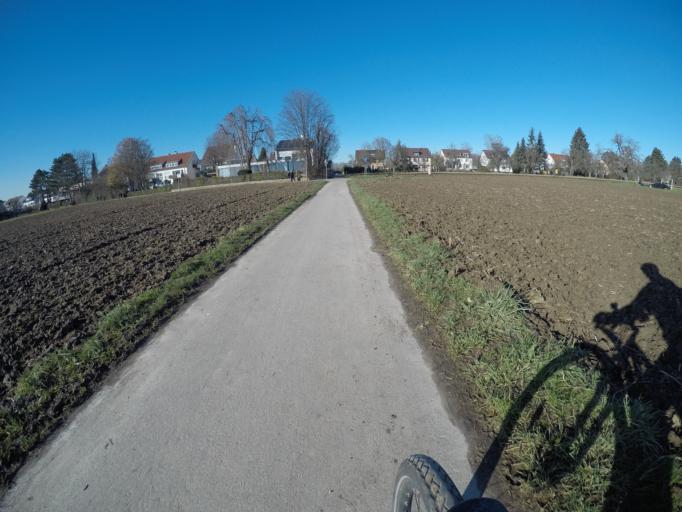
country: DE
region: Baden-Wuerttemberg
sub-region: Regierungsbezirk Stuttgart
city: Leinfelden-Echterdingen
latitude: 48.7379
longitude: 9.1468
